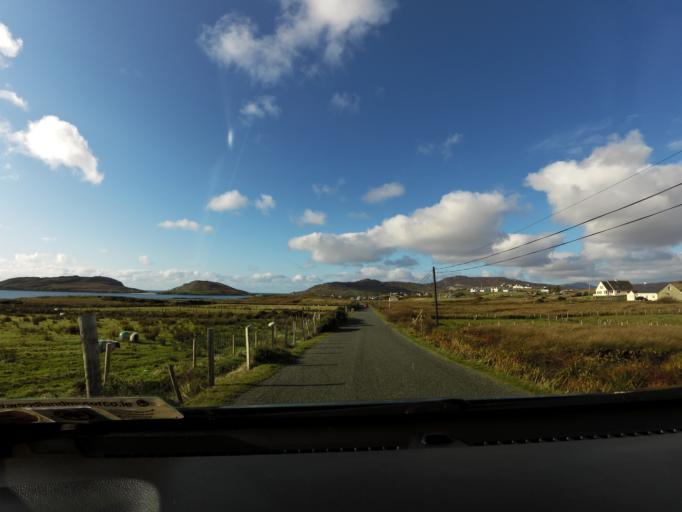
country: IE
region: Connaught
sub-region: Maigh Eo
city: Belmullet
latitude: 53.8684
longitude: -9.9101
